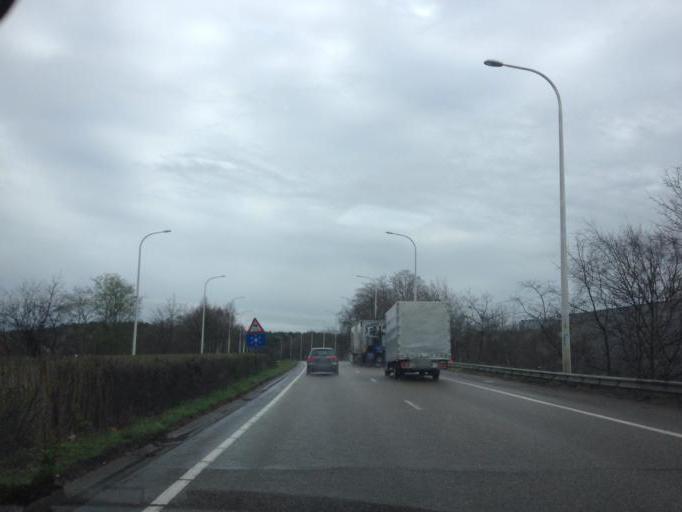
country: BE
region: Flanders
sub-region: Provincie Limburg
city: Genk
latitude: 50.9545
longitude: 5.4828
